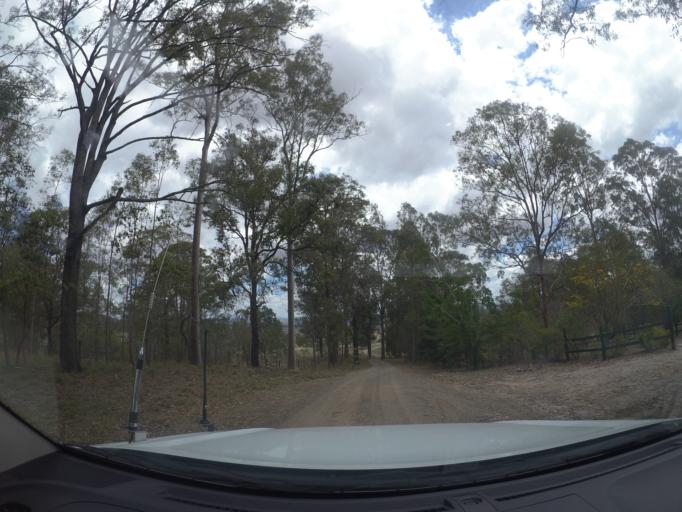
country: AU
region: Queensland
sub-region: Logan
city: Cedar Vale
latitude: -27.9169
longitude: 153.0361
